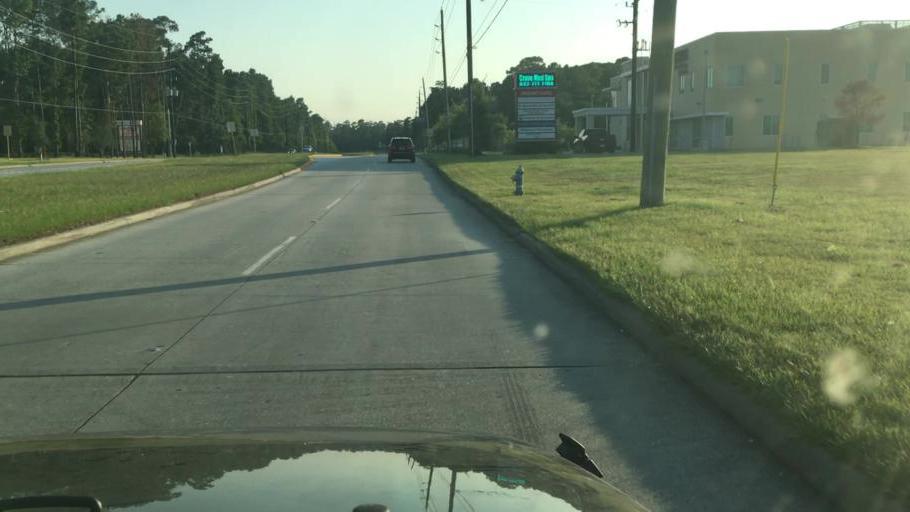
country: US
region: Texas
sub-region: Harris County
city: Atascocita
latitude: 29.9802
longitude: -95.1652
